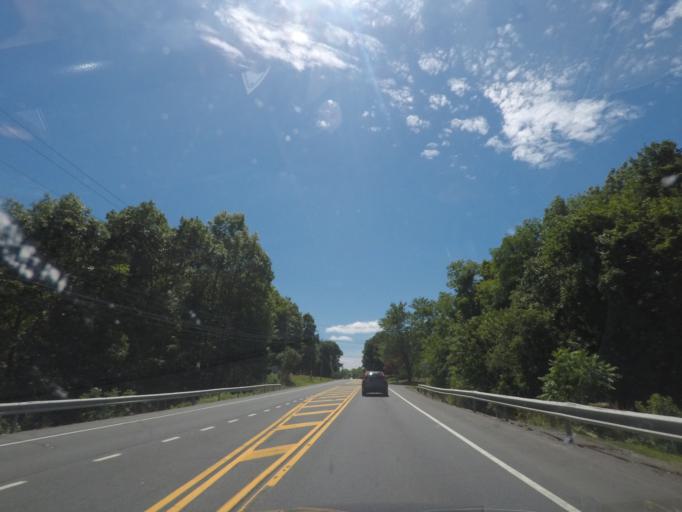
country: US
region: New York
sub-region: Albany County
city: Menands
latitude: 42.6760
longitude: -73.6908
